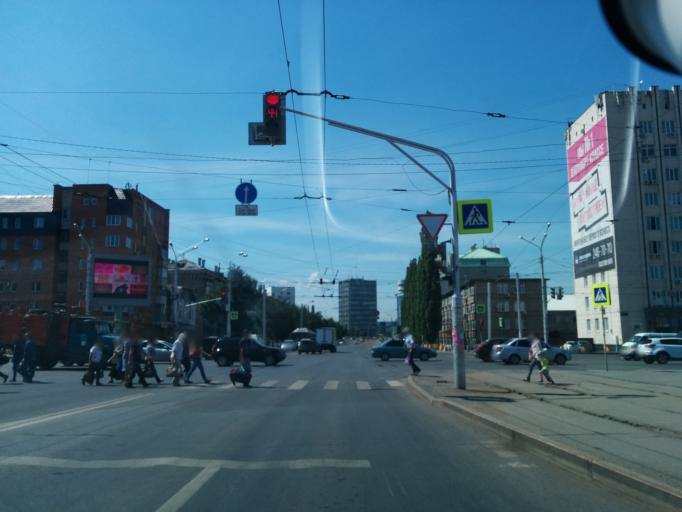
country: RU
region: Bashkortostan
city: Ufa
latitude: 54.7501
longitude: 55.9859
